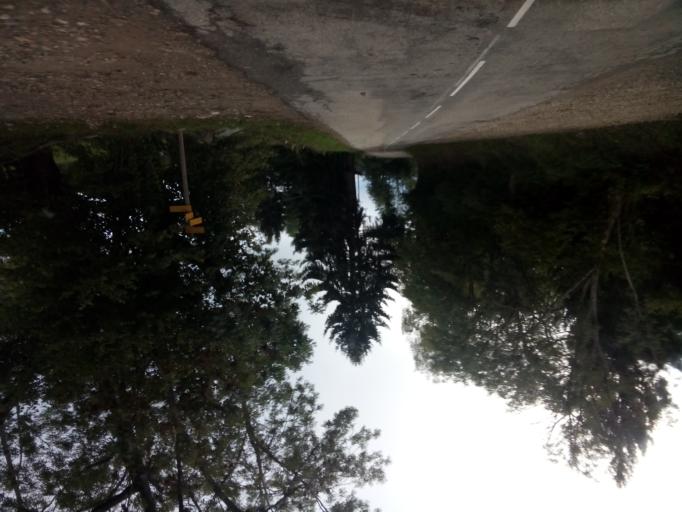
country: FR
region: Rhone-Alpes
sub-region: Departement de l'Isere
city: Le Champ-pres-Froges
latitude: 45.2551
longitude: 5.9704
